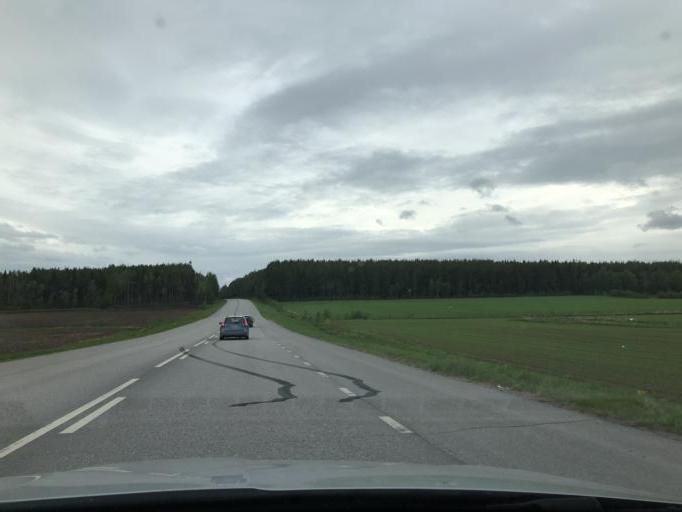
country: SE
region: Norrbotten
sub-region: Pitea Kommun
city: Norrfjarden
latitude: 65.3711
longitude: 21.4192
